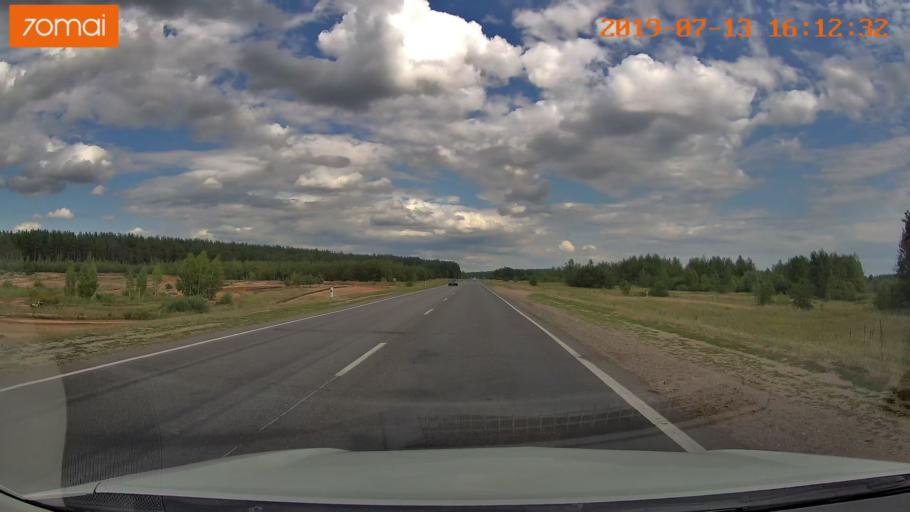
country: BY
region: Mogilev
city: Babruysk
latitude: 53.1666
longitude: 29.2826
